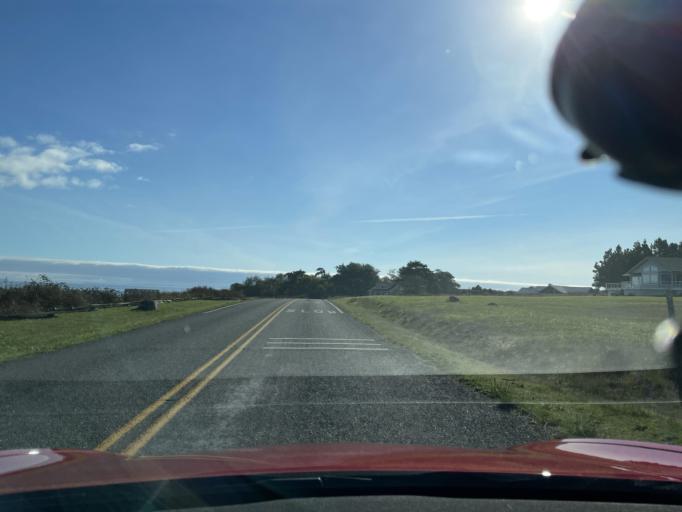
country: US
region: Washington
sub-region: San Juan County
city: Friday Harbor
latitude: 48.4559
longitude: -122.9634
